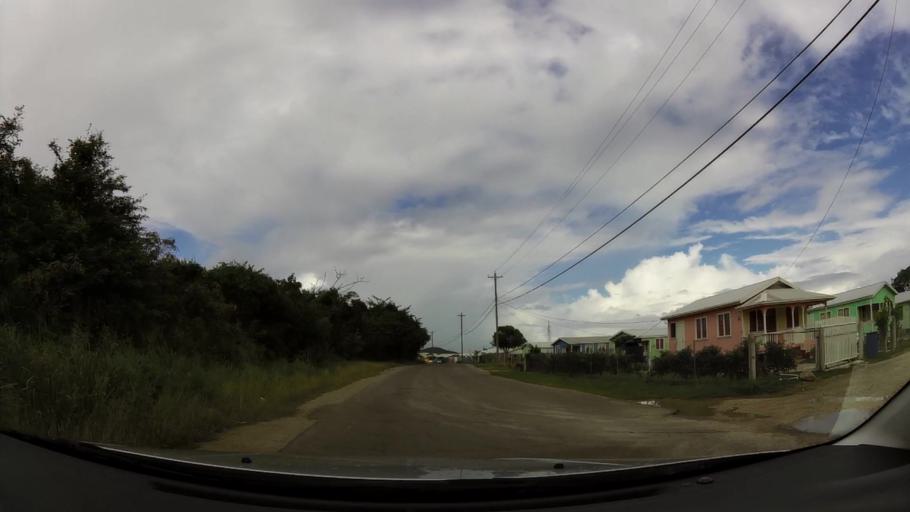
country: AG
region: Saint John
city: Potters Village
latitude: 17.0943
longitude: -61.8136
